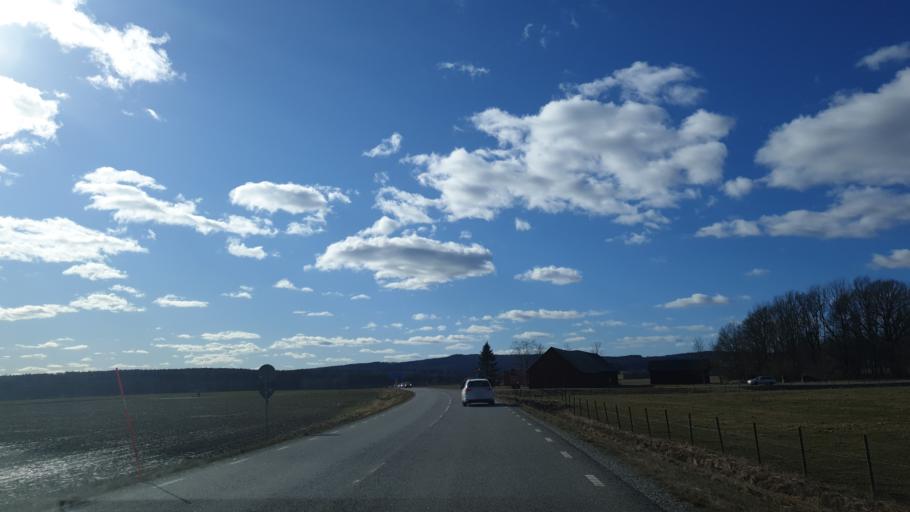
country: SE
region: OErebro
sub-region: Orebro Kommun
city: Garphyttan
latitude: 59.3410
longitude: 15.0489
